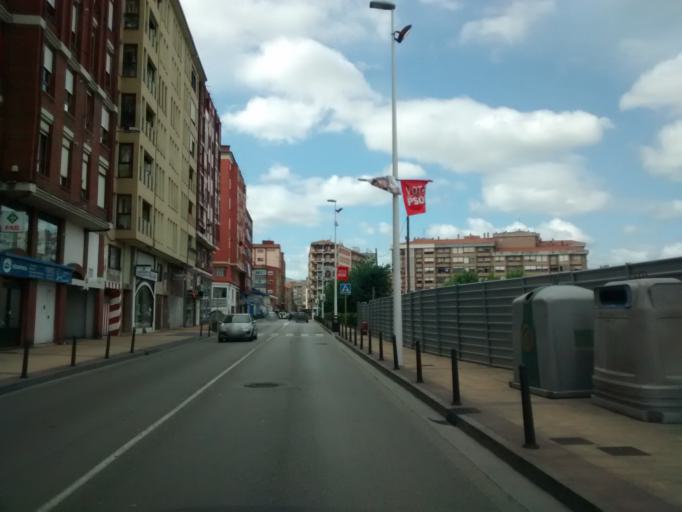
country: ES
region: Cantabria
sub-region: Provincia de Cantabria
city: Torrelavega
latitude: 43.3560
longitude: -4.0465
